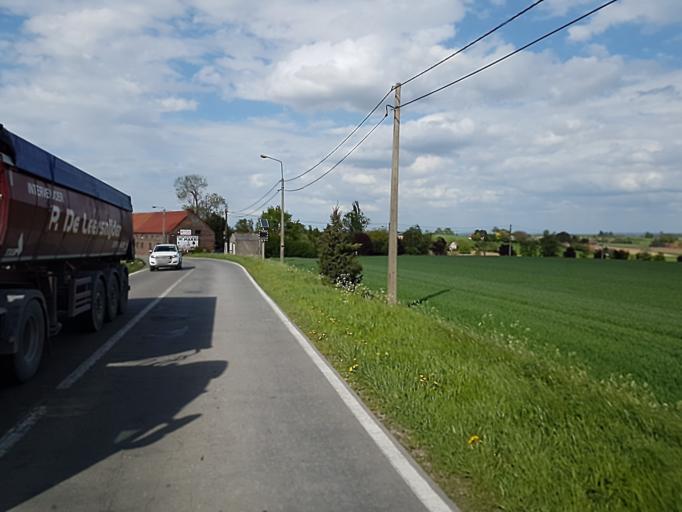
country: BE
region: Wallonia
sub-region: Province du Hainaut
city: Celles
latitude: 50.6555
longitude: 3.4344
